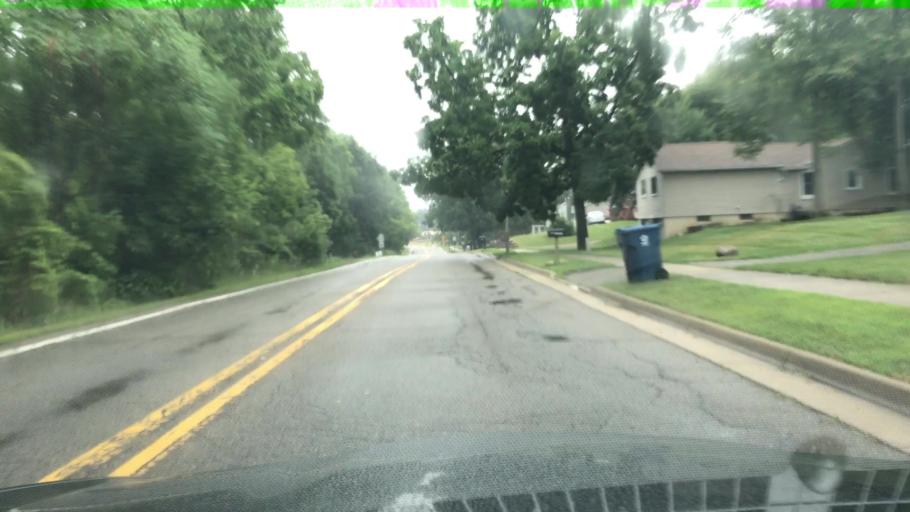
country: US
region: Michigan
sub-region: Oakland County
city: Auburn Hills
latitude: 42.7257
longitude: -83.2733
